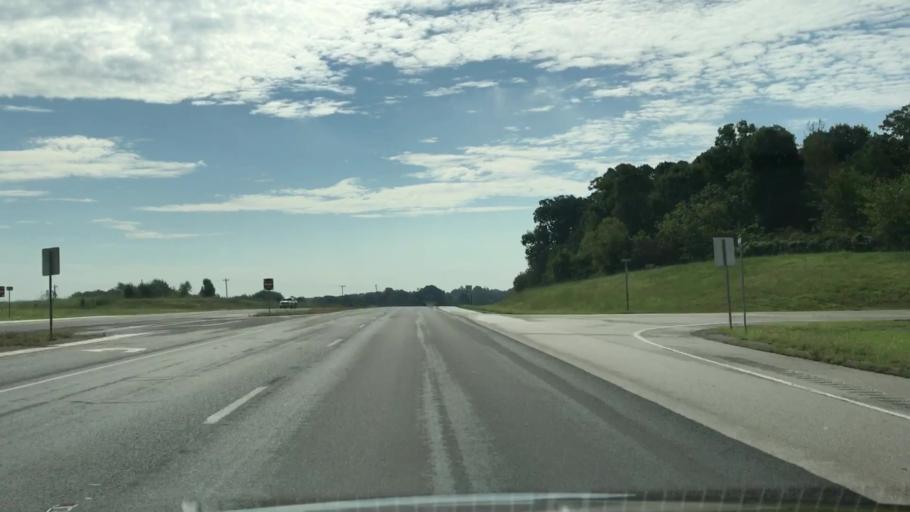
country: US
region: Kentucky
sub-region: Warren County
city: Plano
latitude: 36.8600
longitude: -86.3444
